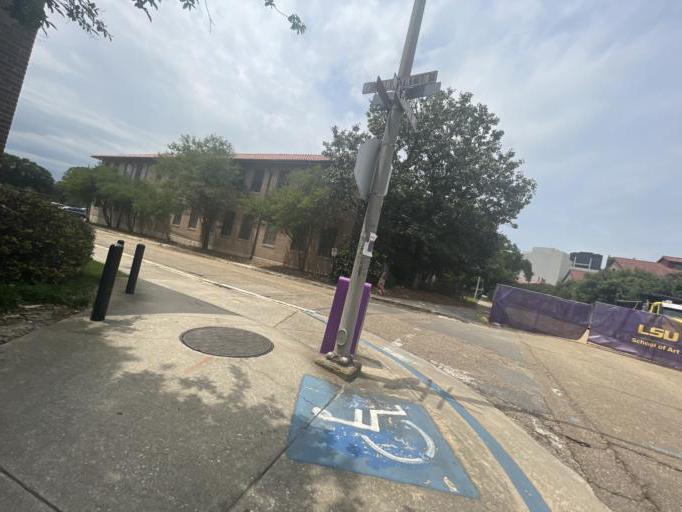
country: US
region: Louisiana
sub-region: East Baton Rouge Parish
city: Baton Rouge
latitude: 30.4109
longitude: -91.1794
